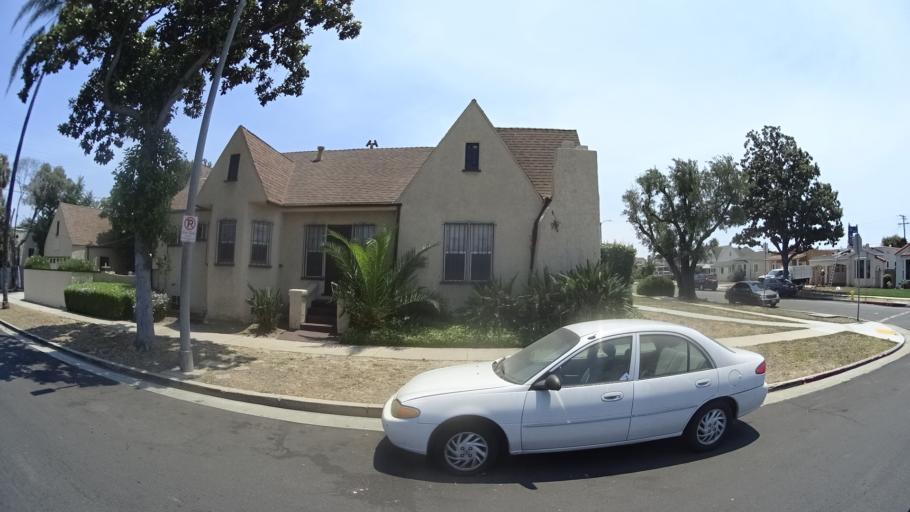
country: US
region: California
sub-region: Los Angeles County
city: Westmont
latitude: 33.9728
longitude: -118.3022
